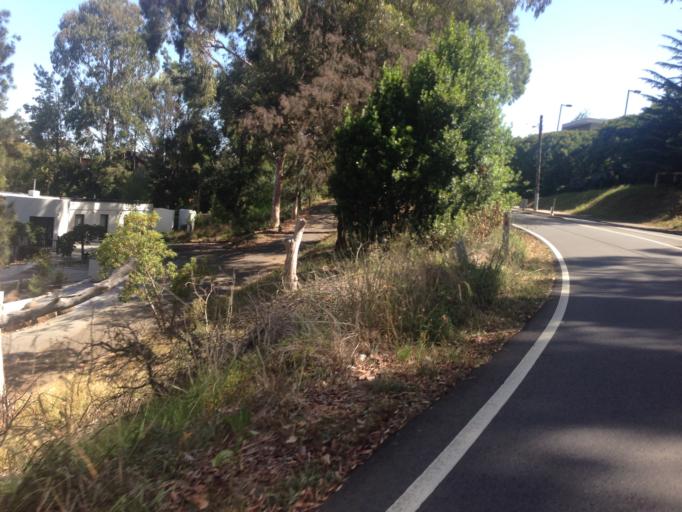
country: AU
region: Victoria
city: Ivanhoe East
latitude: -37.7784
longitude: 145.0436
